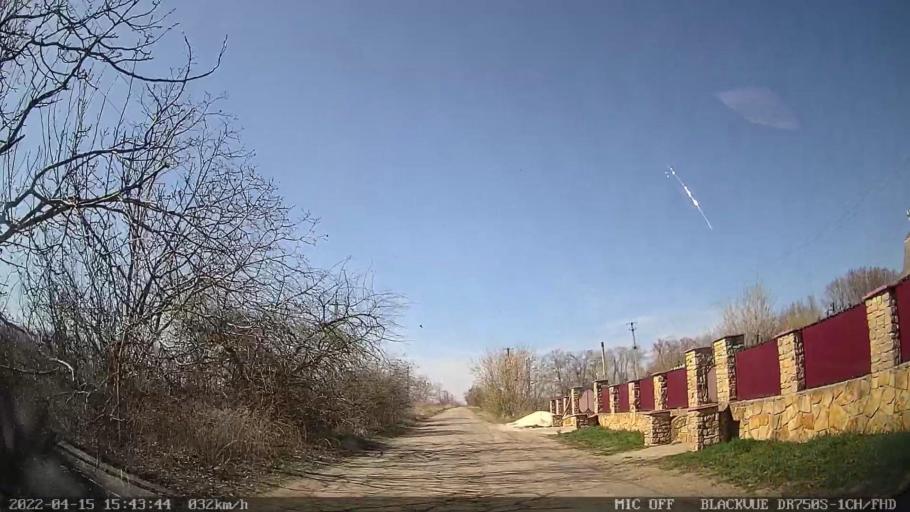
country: MD
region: Raionul Ocnita
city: Otaci
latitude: 48.3666
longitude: 27.9251
